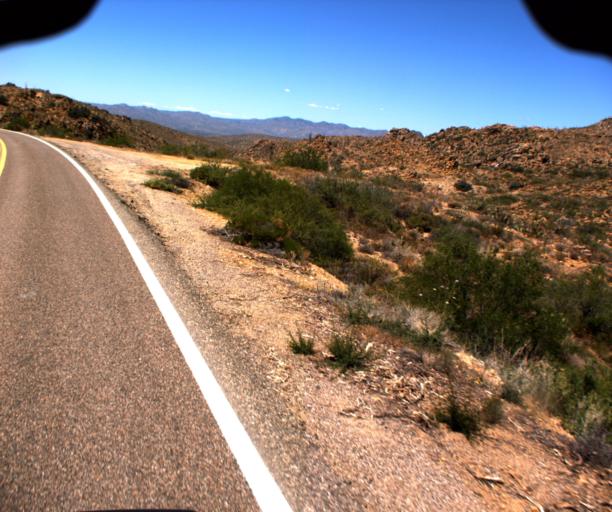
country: US
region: Arizona
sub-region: Yavapai County
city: Bagdad
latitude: 34.4459
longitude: -112.9658
